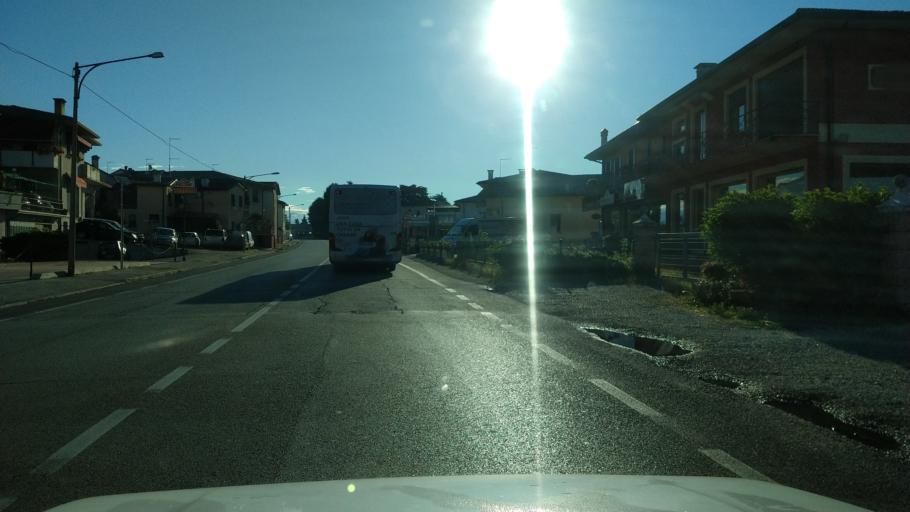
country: IT
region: Veneto
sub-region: Provincia di Vicenza
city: Marostica
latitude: 45.7561
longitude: 11.6829
